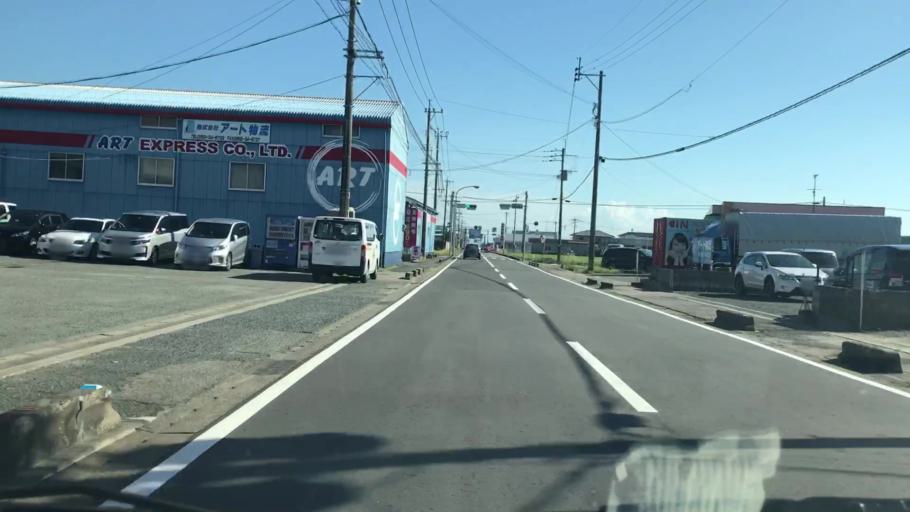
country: JP
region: Saga Prefecture
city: Okawa
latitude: 33.2091
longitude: 130.3354
